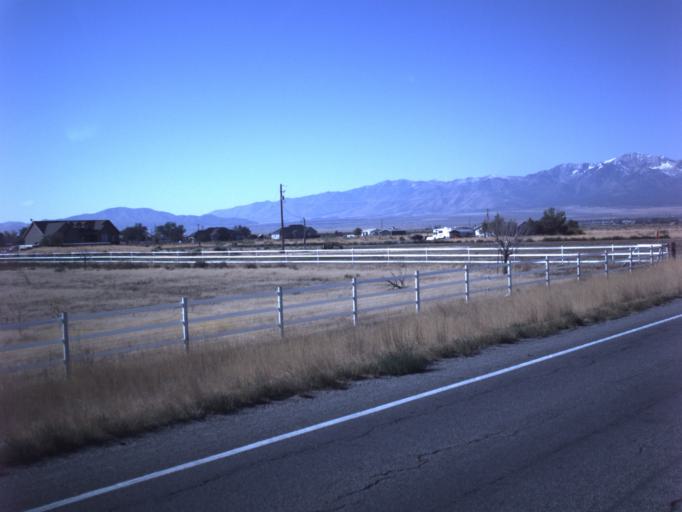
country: US
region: Utah
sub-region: Tooele County
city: Grantsville
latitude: 40.6053
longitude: -112.3907
